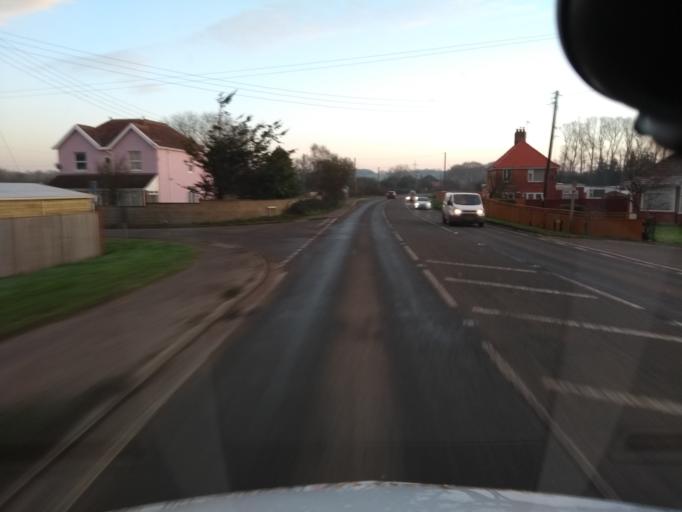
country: GB
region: England
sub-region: Somerset
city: Puriton
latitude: 51.1451
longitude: -2.9708
